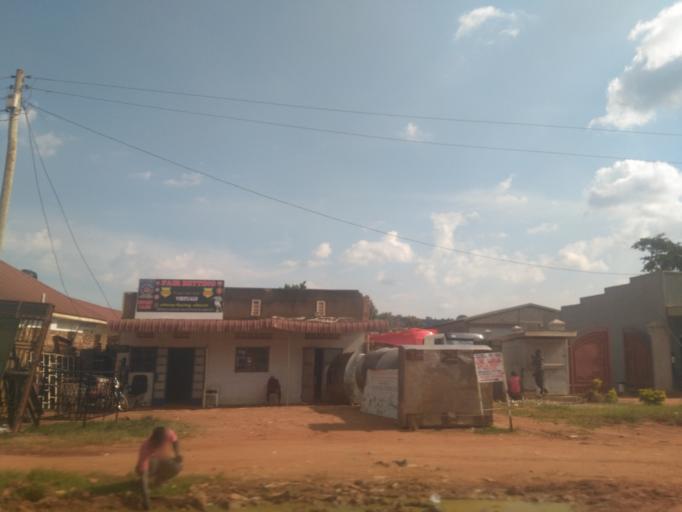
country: UG
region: Central Region
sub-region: Wakiso District
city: Kajansi
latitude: 0.2784
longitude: 32.4777
